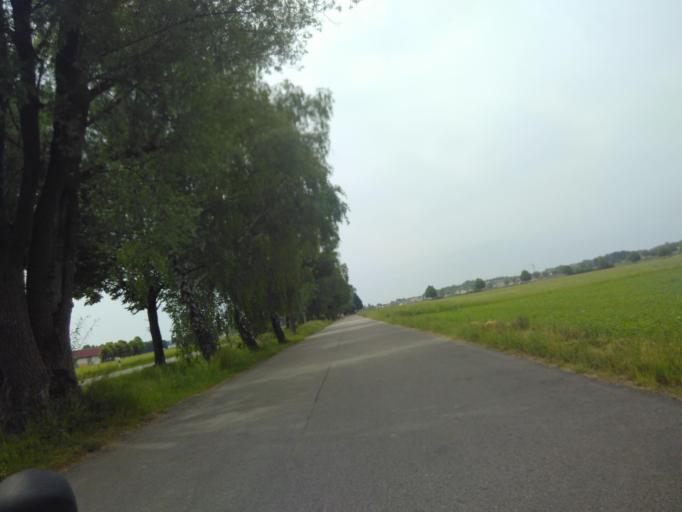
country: DE
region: Bavaria
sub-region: Upper Bavaria
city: Eichenau
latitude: 48.1550
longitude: 11.3130
